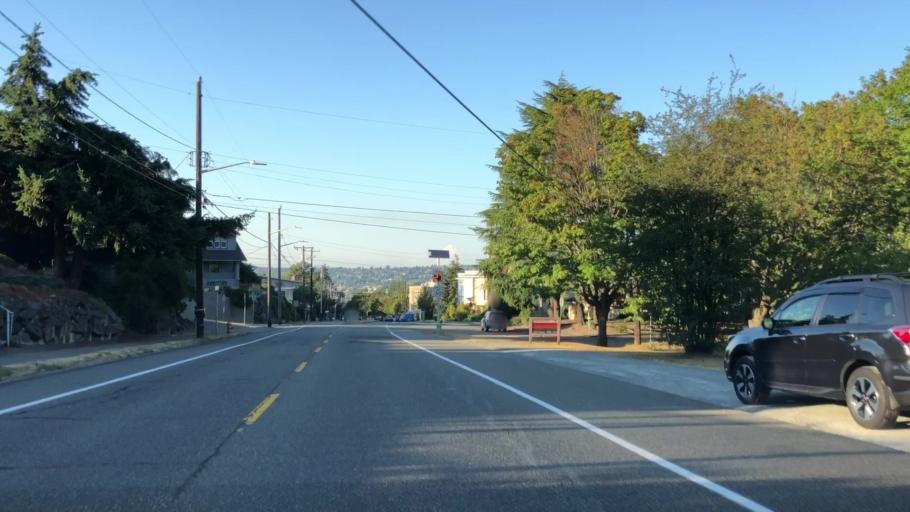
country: US
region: Washington
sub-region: King County
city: Seattle
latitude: 47.6355
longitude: -122.3902
